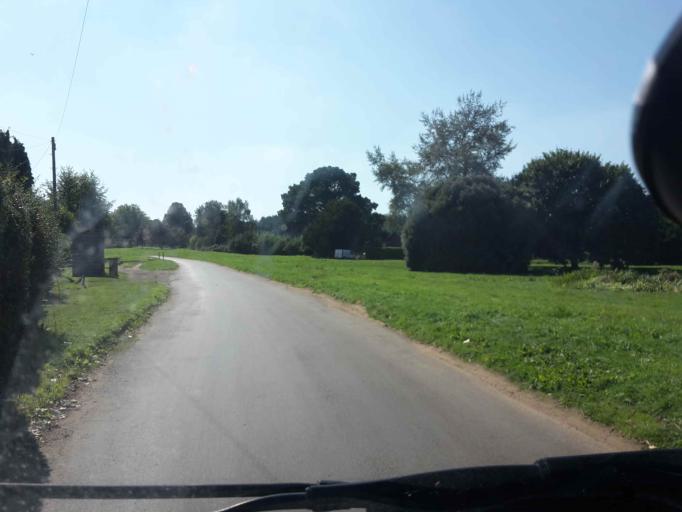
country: GB
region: England
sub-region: Surrey
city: Chilworth
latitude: 51.1988
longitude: -0.4854
